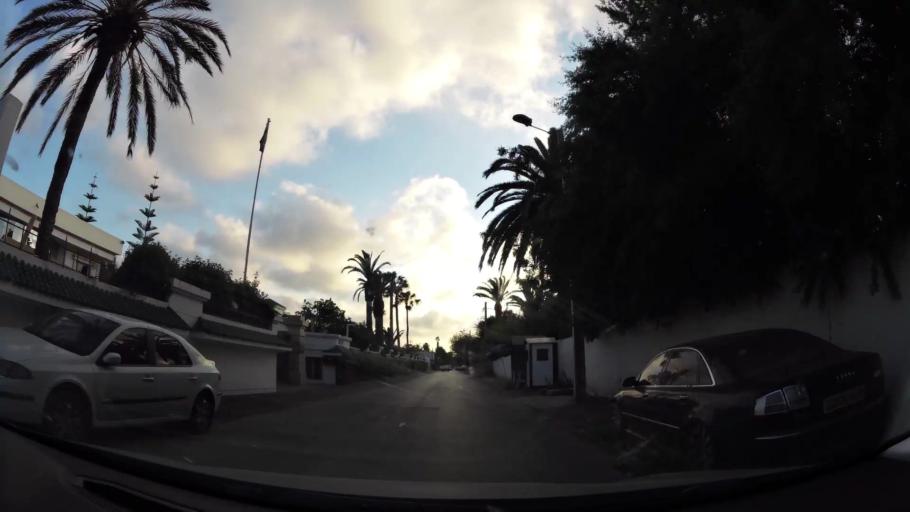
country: MA
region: Rabat-Sale-Zemmour-Zaer
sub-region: Rabat
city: Rabat
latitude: 33.9772
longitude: -6.8315
